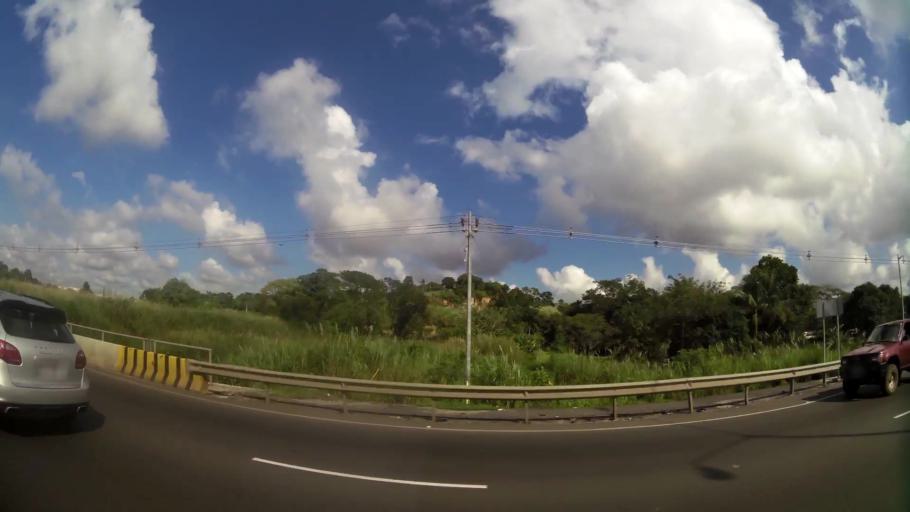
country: PA
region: Panama
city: Nuevo Arraijan
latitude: 8.9162
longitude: -79.7118
